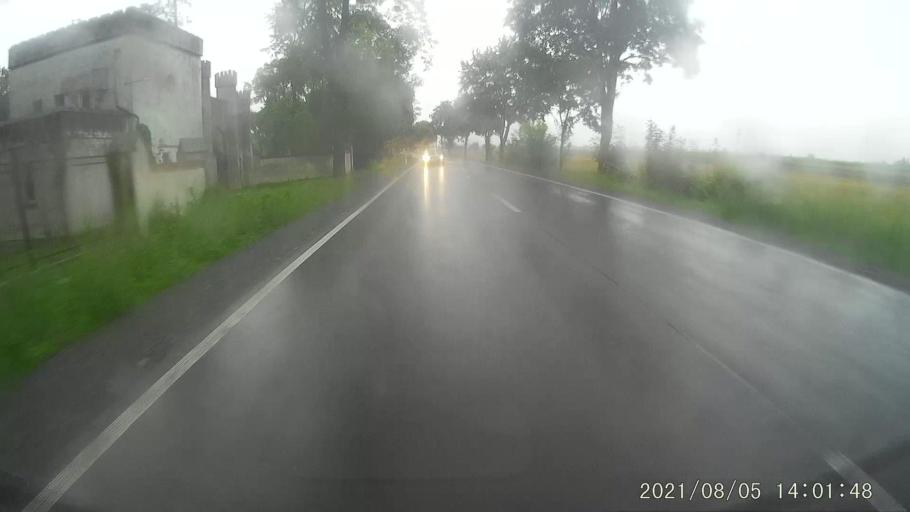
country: PL
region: Opole Voivodeship
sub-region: Powiat krapkowicki
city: Strzeleczki
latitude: 50.4505
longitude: 17.8866
